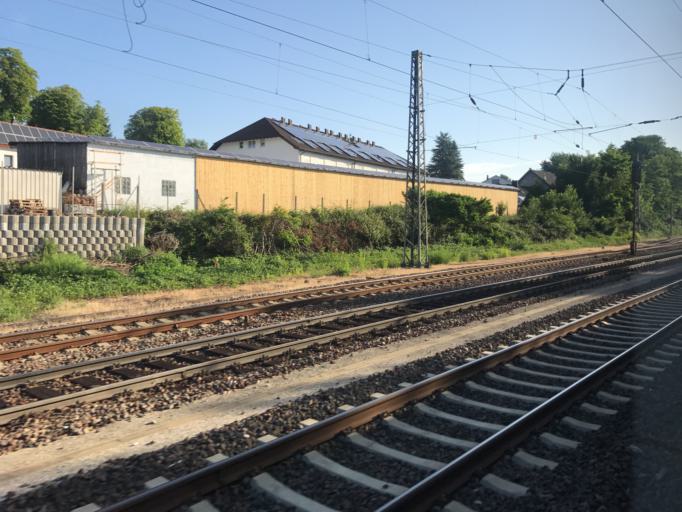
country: DE
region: Saarland
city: Sulzbach
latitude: 49.2755
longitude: 7.0230
